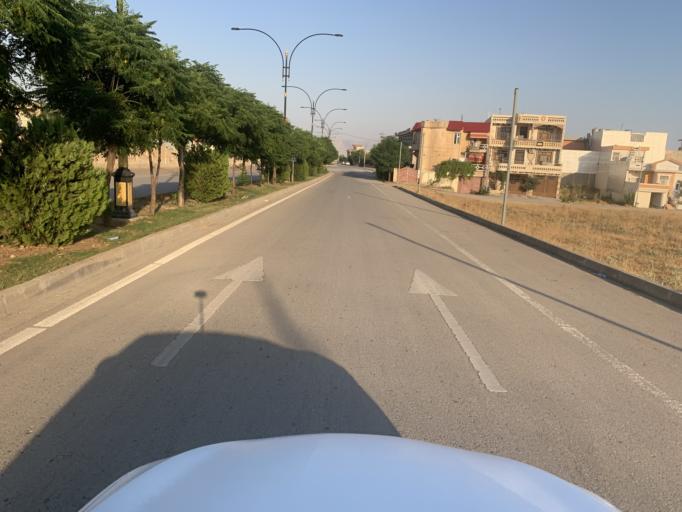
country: IQ
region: As Sulaymaniyah
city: Raniye
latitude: 36.2403
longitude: 44.8759
